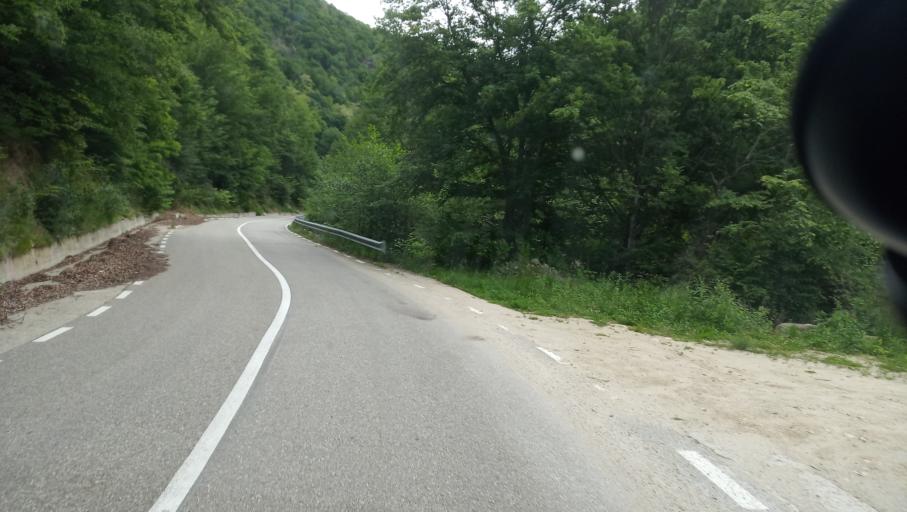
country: RO
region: Caras-Severin
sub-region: Comuna Slatina-Timis
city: Slatina-Timis
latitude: 45.2574
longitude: 22.2520
